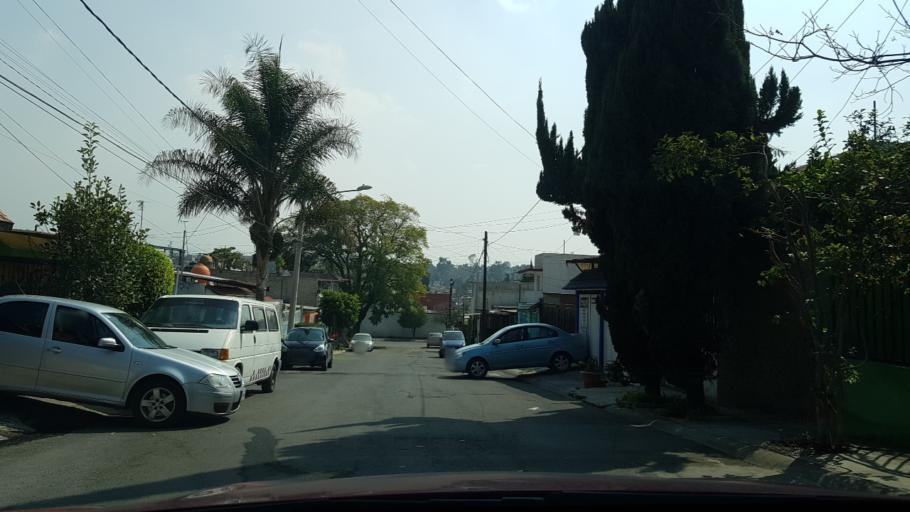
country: MX
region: Mexico
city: Cuautitlan Izcalli
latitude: 19.6453
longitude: -99.2131
